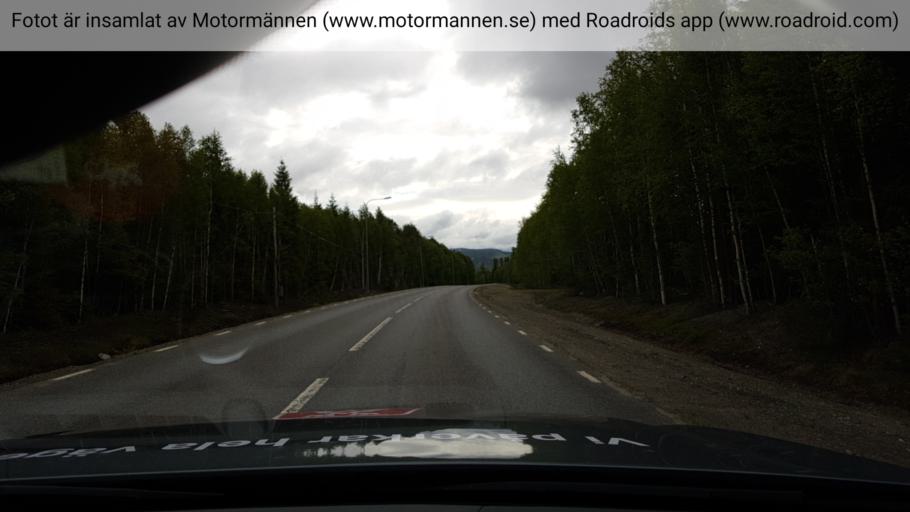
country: NO
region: Nord-Trondelag
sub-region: Lierne
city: Sandvika
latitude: 64.4794
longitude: 14.1099
